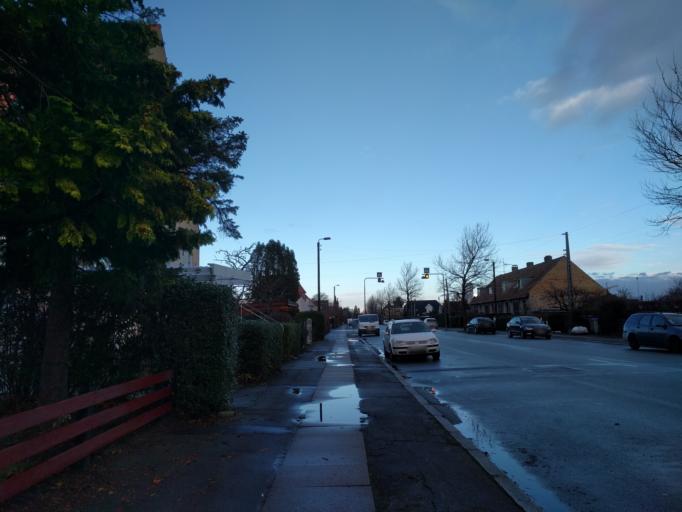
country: DK
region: Capital Region
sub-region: Tarnby Kommune
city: Tarnby
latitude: 55.6532
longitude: 12.6314
